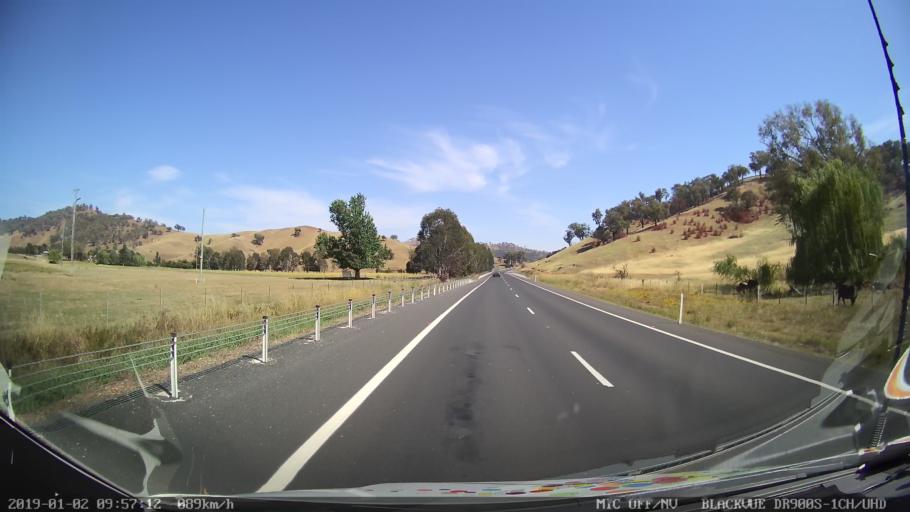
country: AU
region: New South Wales
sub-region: Tumut Shire
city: Tumut
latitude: -35.2084
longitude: 148.1677
